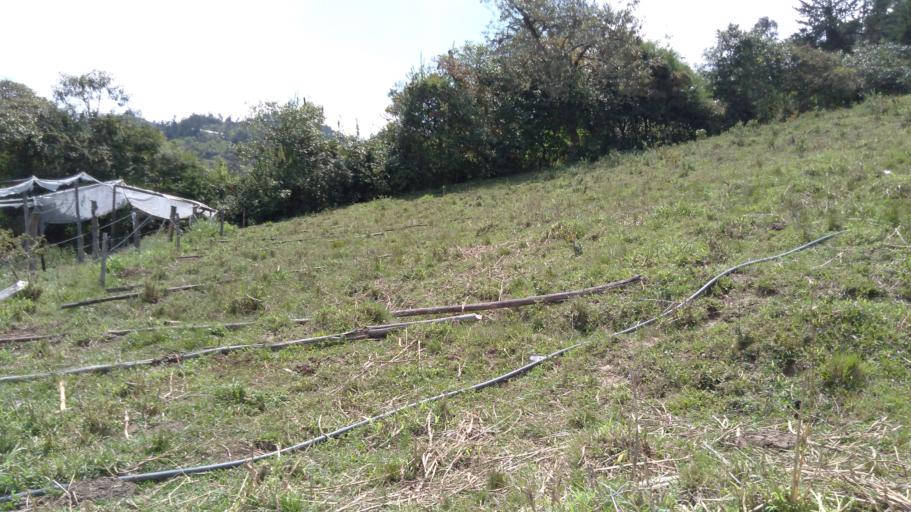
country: CO
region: Cundinamarca
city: Tenza
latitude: 5.0607
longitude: -73.4346
